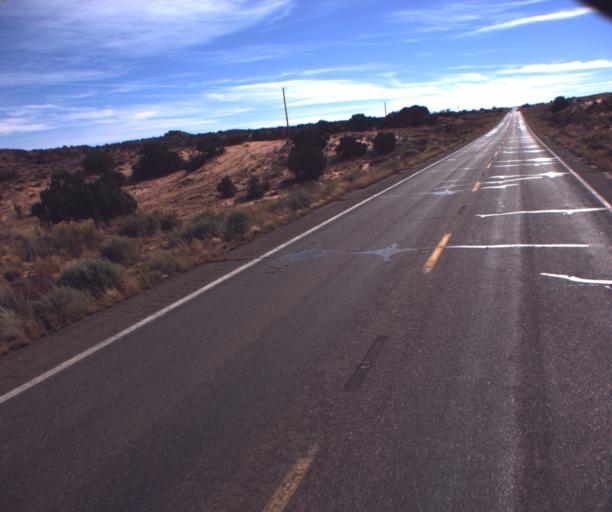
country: US
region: Arizona
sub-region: Coconino County
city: Kaibito
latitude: 36.6048
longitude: -111.1767
